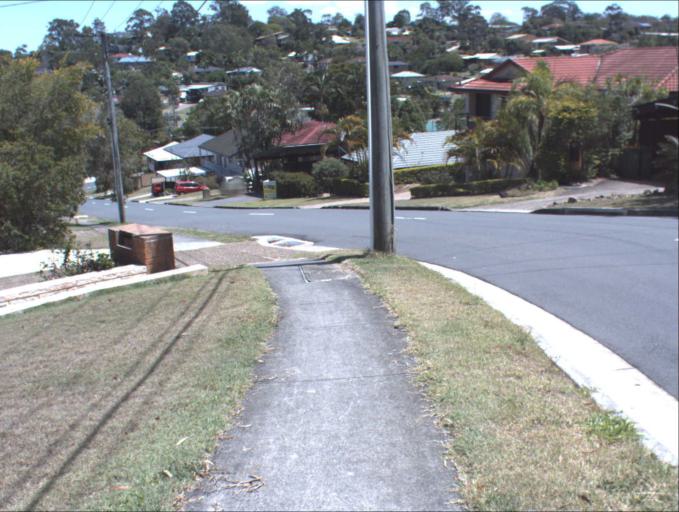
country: AU
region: Queensland
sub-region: Logan
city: Springwood
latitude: -27.6044
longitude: 153.1288
